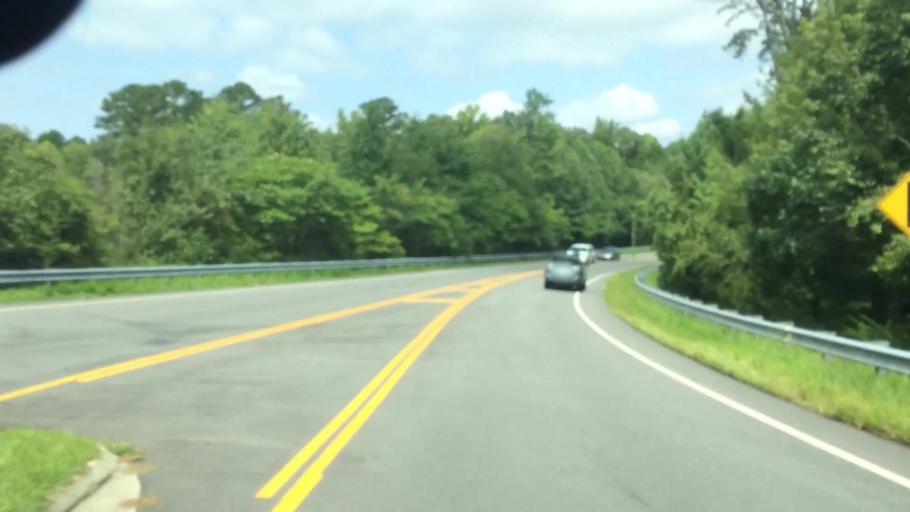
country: US
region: Virginia
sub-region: James City County
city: Williamsburg
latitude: 37.2573
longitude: -76.7879
